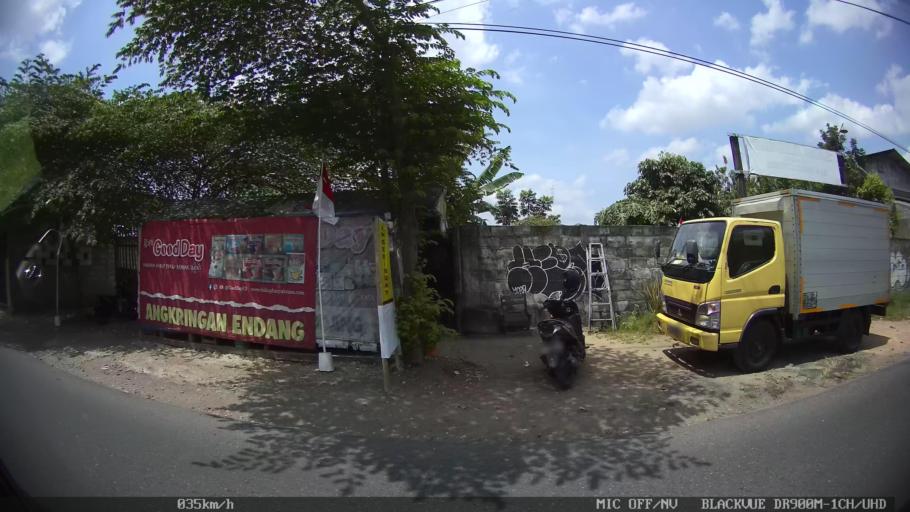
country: ID
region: Daerah Istimewa Yogyakarta
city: Gamping Lor
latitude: -7.8045
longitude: 110.3411
